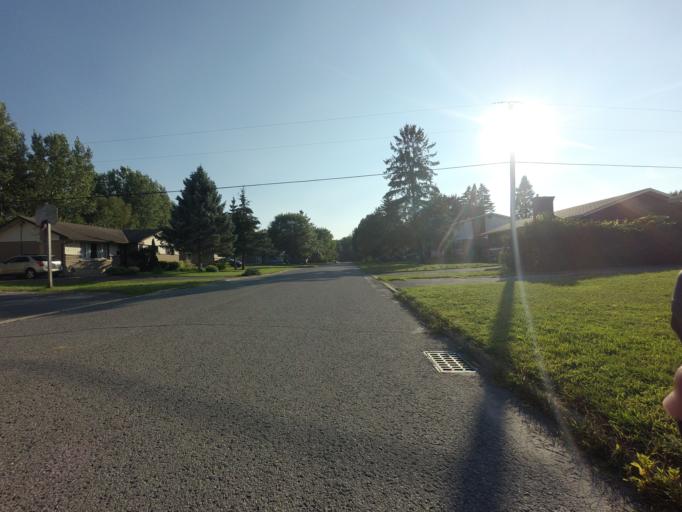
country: CA
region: Ontario
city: Bells Corners
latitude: 45.3252
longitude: -75.7642
